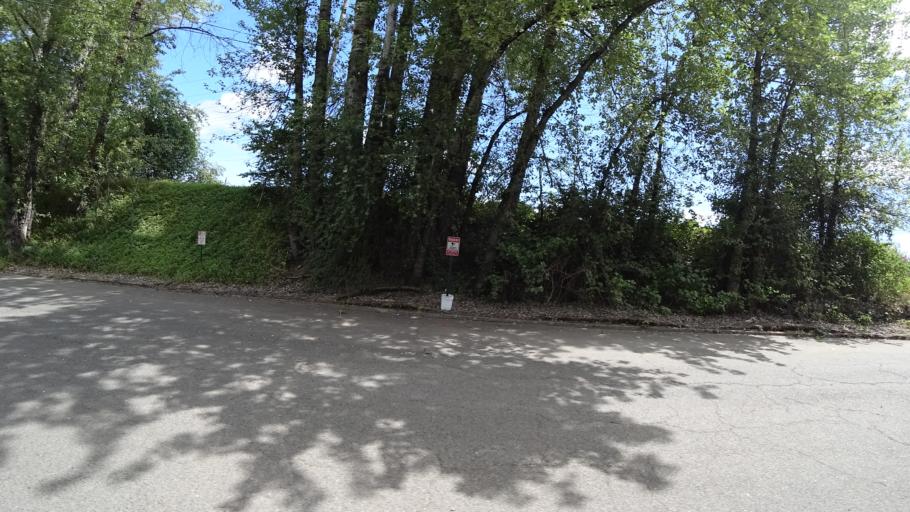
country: US
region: Oregon
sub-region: Washington County
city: West Haven
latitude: 45.6092
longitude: -122.7683
